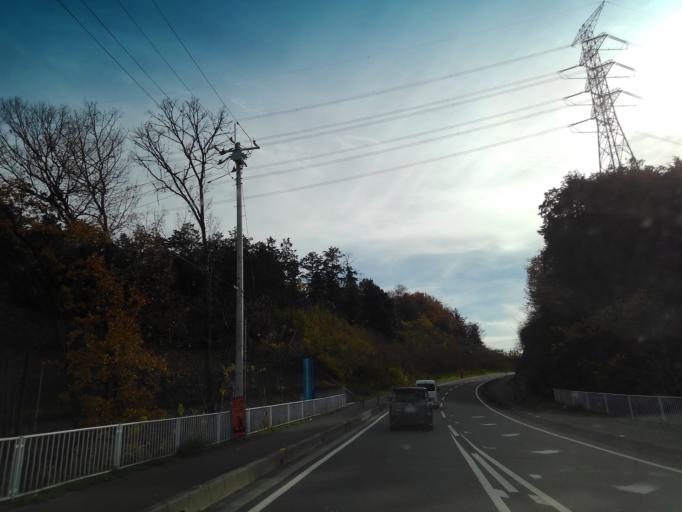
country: JP
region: Saitama
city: Morohongo
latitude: 35.9257
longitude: 139.3212
